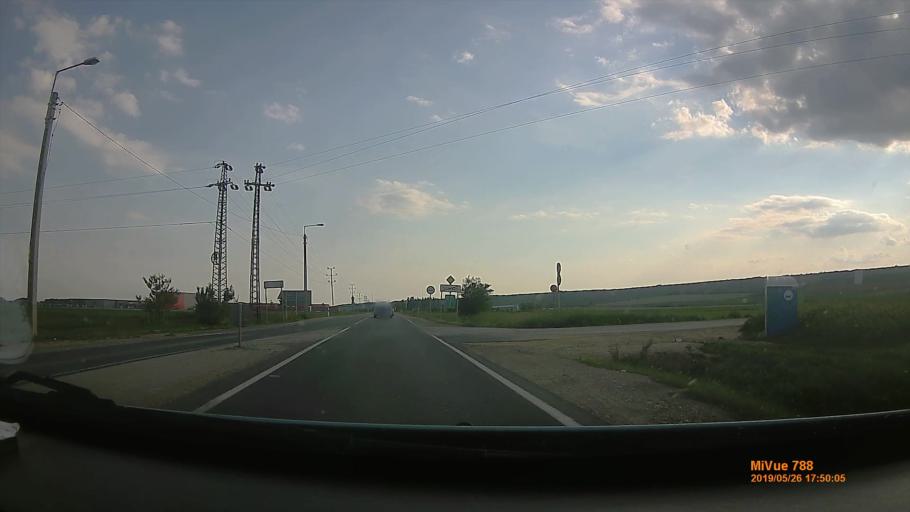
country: HU
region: Borsod-Abauj-Zemplen
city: Szikszo
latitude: 48.1850
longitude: 20.9219
